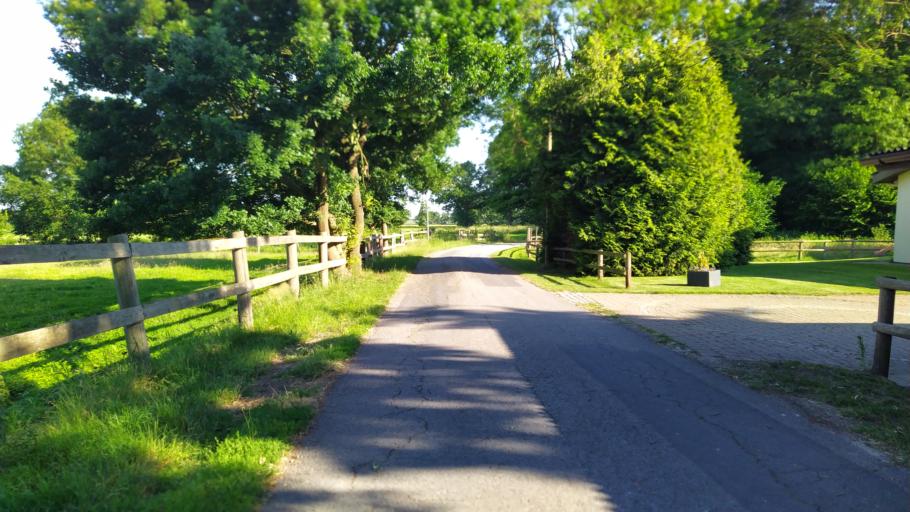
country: DE
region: Lower Saxony
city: Lintig
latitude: 53.5959
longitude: 8.9295
